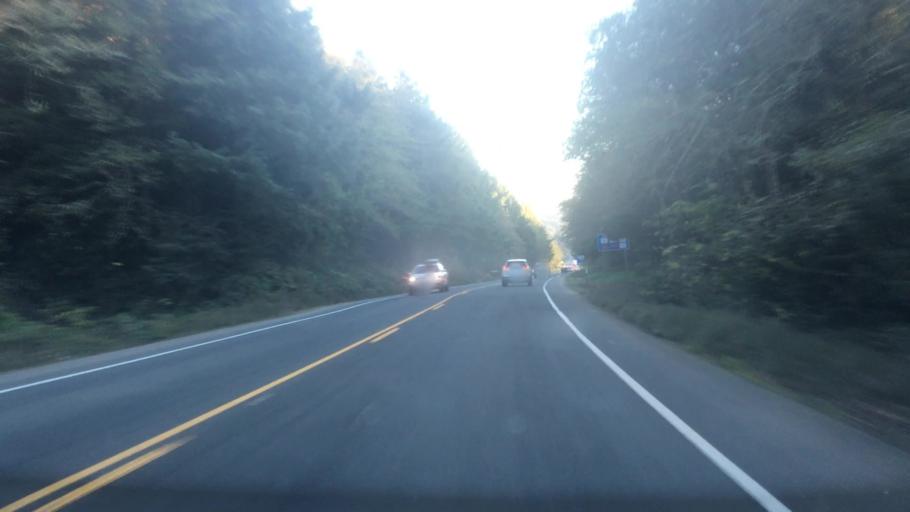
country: US
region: Oregon
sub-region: Clatsop County
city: Cannon Beach
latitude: 45.8786
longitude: -123.9576
